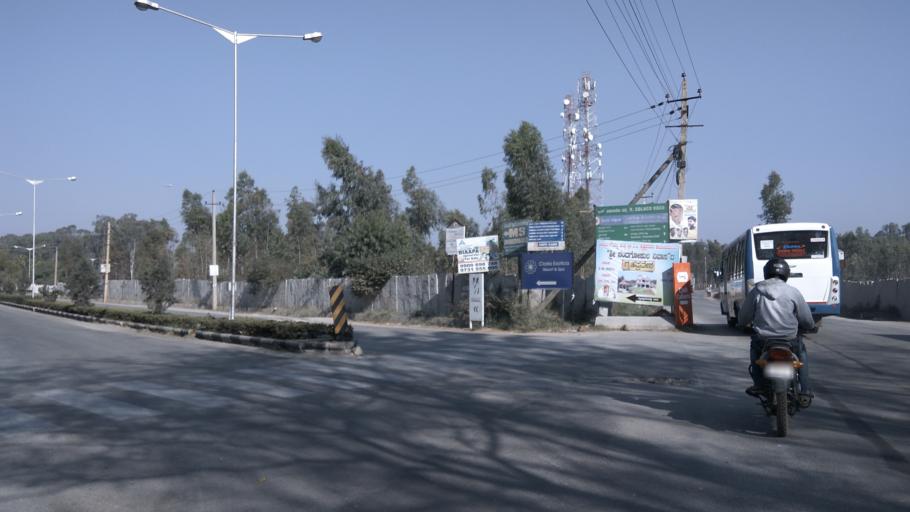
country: IN
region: Karnataka
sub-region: Bangalore Rural
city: Devanhalli
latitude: 13.1932
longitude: 77.6458
